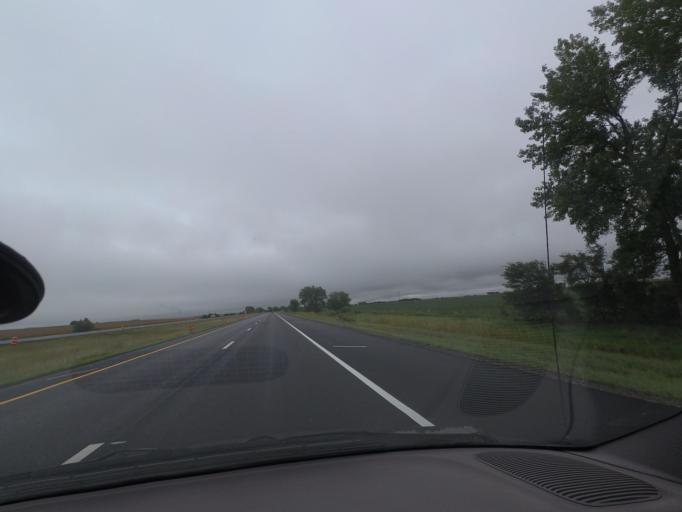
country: US
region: Illinois
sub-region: Macon County
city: Harristown
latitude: 39.8366
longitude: -89.1750
